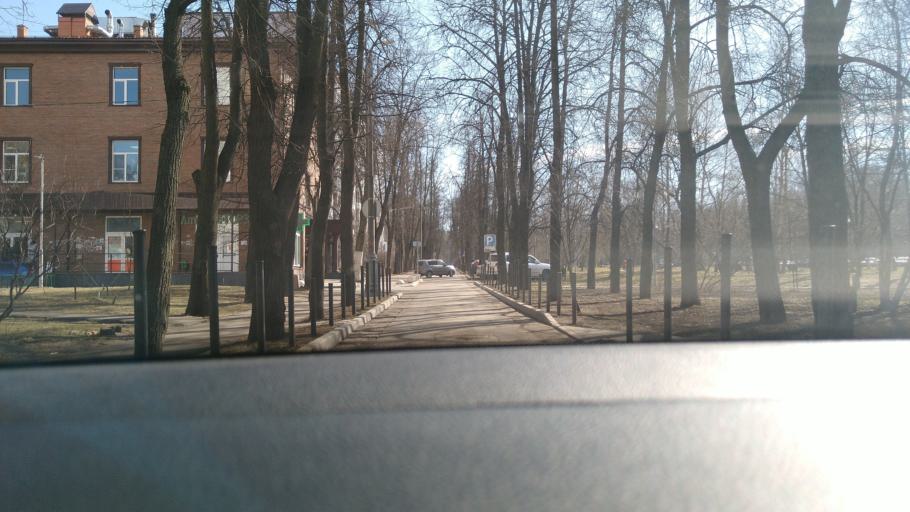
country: RU
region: Moscow
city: Rublevo
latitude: 55.7842
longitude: 37.3539
